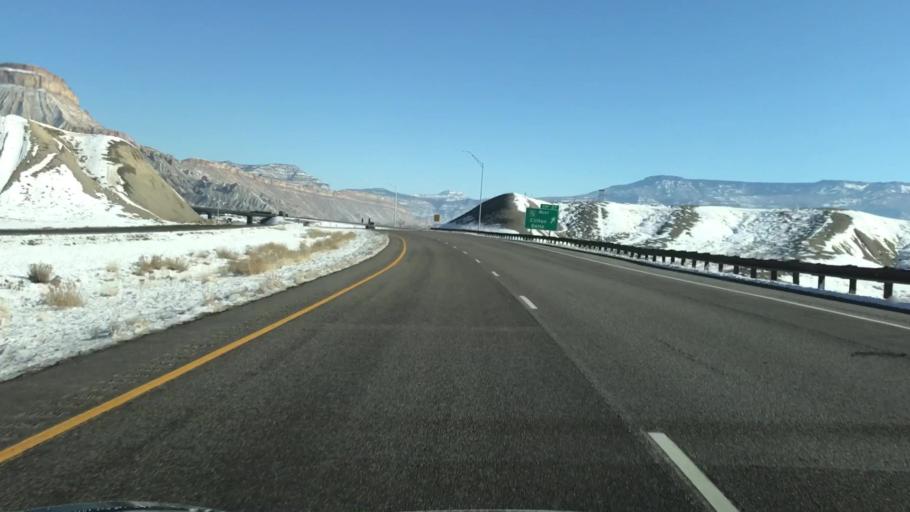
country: US
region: Colorado
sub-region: Mesa County
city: Clifton
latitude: 39.1020
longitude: -108.4527
